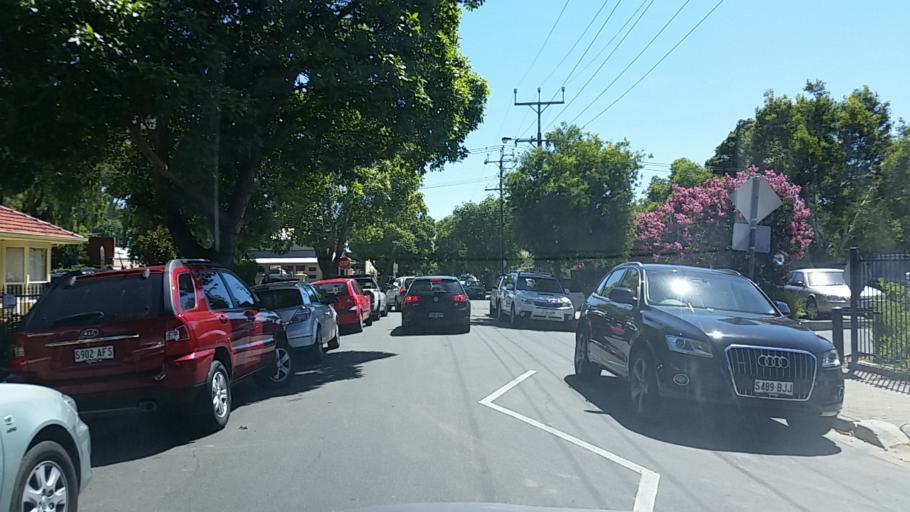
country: AU
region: South Australia
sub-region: Unley
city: Fullarton
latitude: -34.9449
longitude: 138.6191
